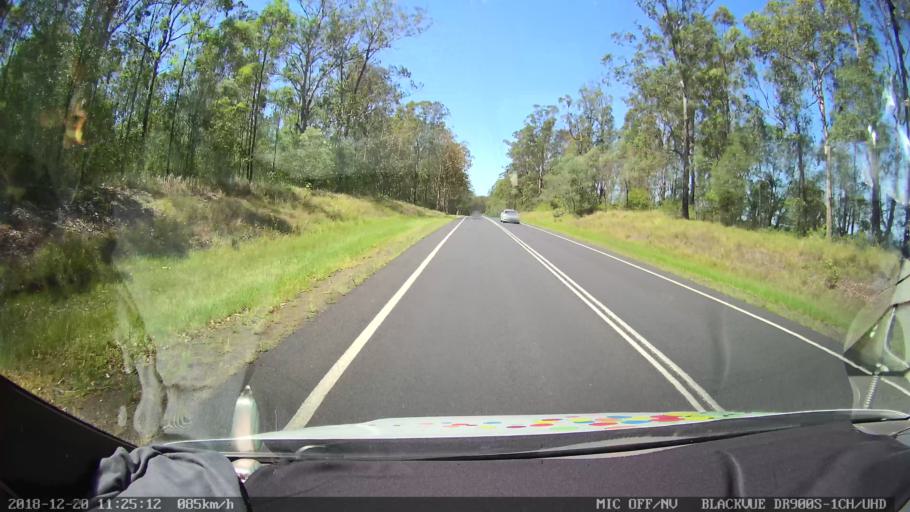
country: AU
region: New South Wales
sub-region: Richmond Valley
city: Casino
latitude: -29.0844
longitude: 153.0007
